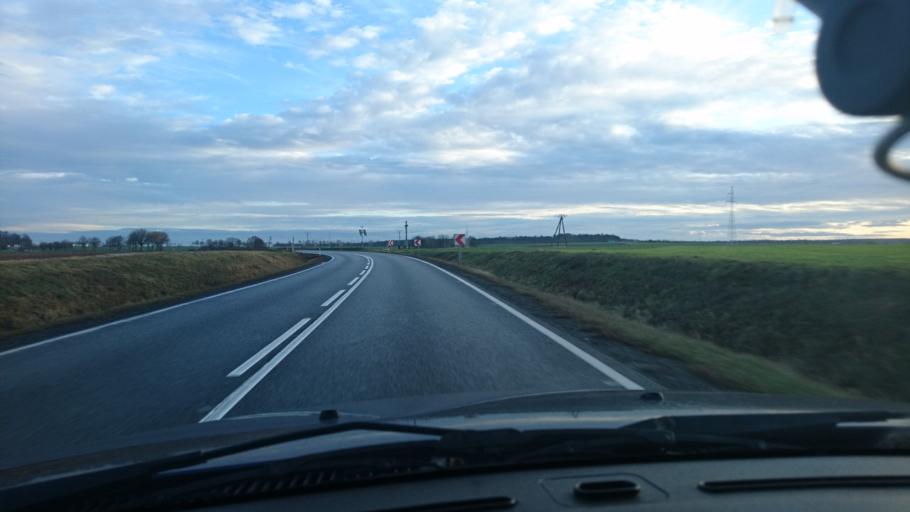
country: PL
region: Greater Poland Voivodeship
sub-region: Powiat kepinski
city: Baranow
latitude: 51.2469
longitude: 18.0182
